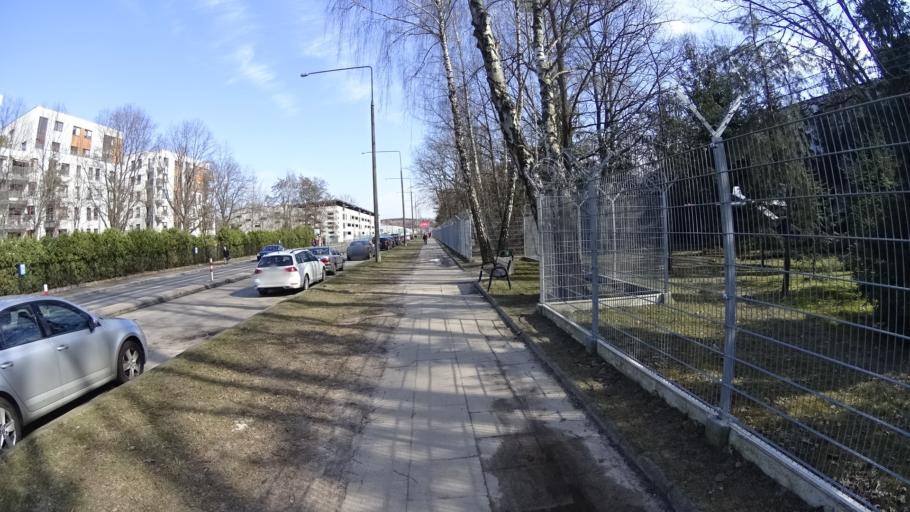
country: PL
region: Masovian Voivodeship
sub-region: Warszawa
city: Bemowo
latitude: 52.2527
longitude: 20.9344
